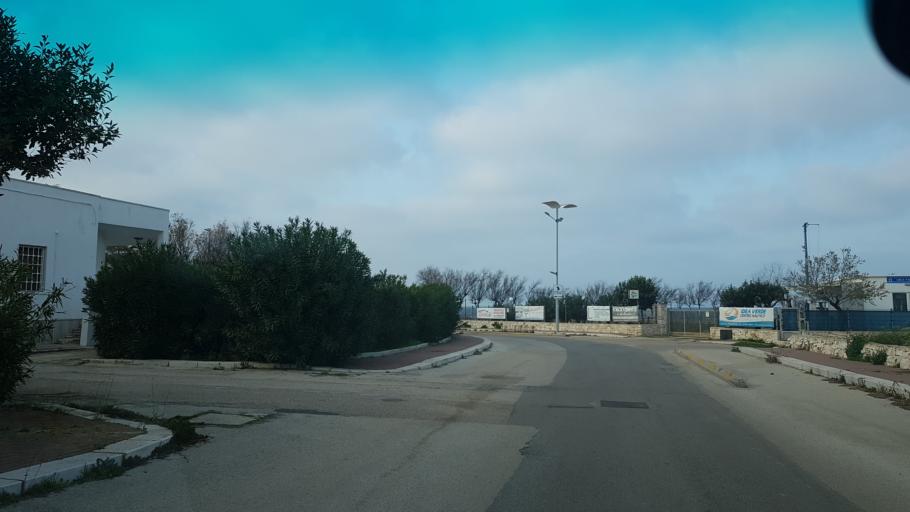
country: IT
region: Apulia
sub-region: Provincia di Brindisi
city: Carovigno
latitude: 40.7388
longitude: 17.7406
